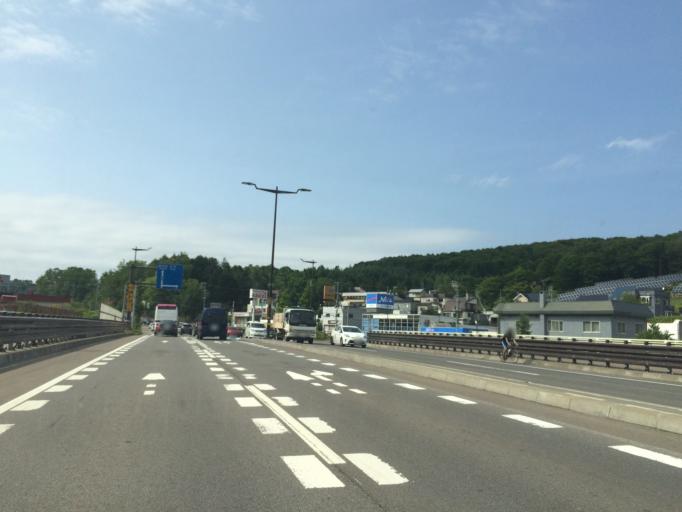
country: JP
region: Hokkaido
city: Otaru
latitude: 43.2176
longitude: 140.9549
